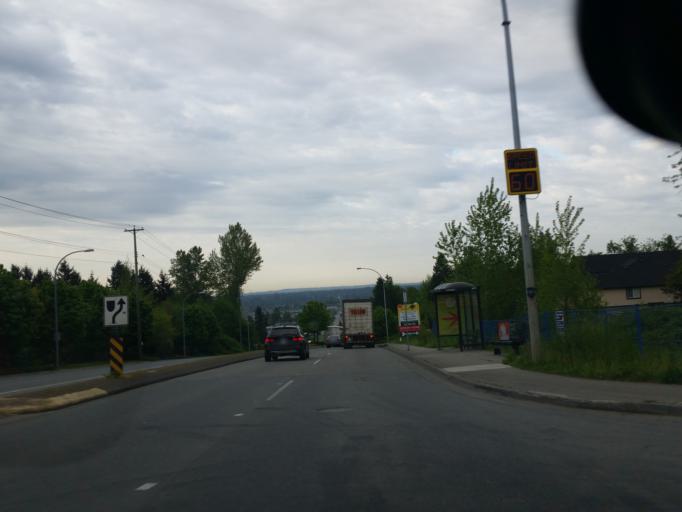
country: CA
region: British Columbia
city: Langley
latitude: 49.1299
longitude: -122.6686
